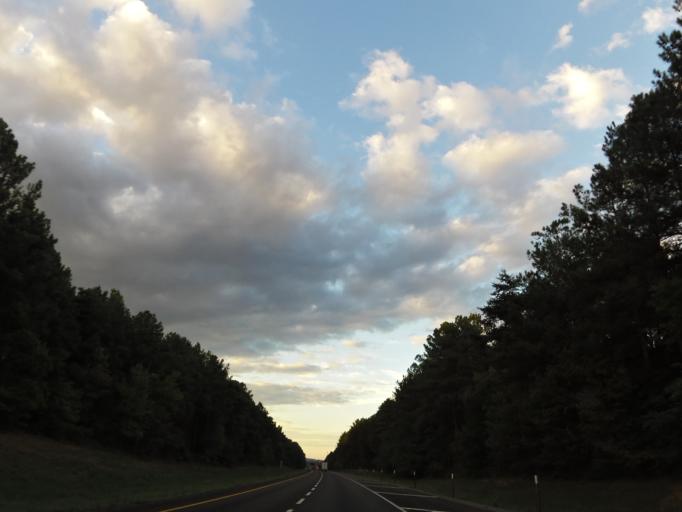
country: US
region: Tennessee
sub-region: Bradley County
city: Hopewell
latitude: 35.2777
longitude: -84.8199
